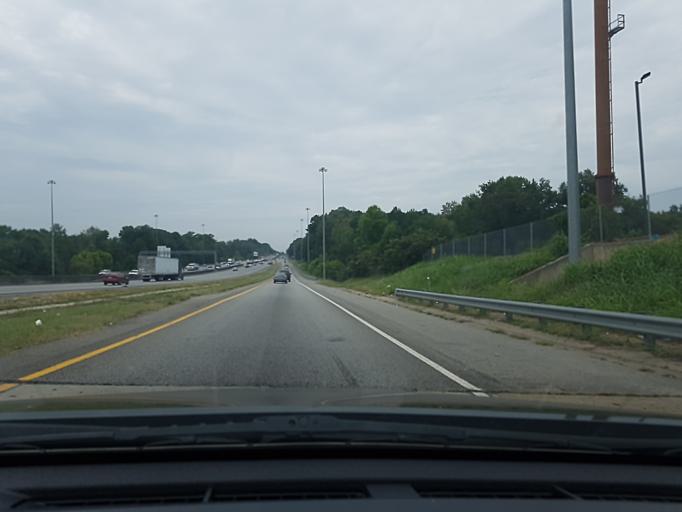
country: US
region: Georgia
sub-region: Clayton County
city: Morrow
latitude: 33.5782
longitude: -84.3469
